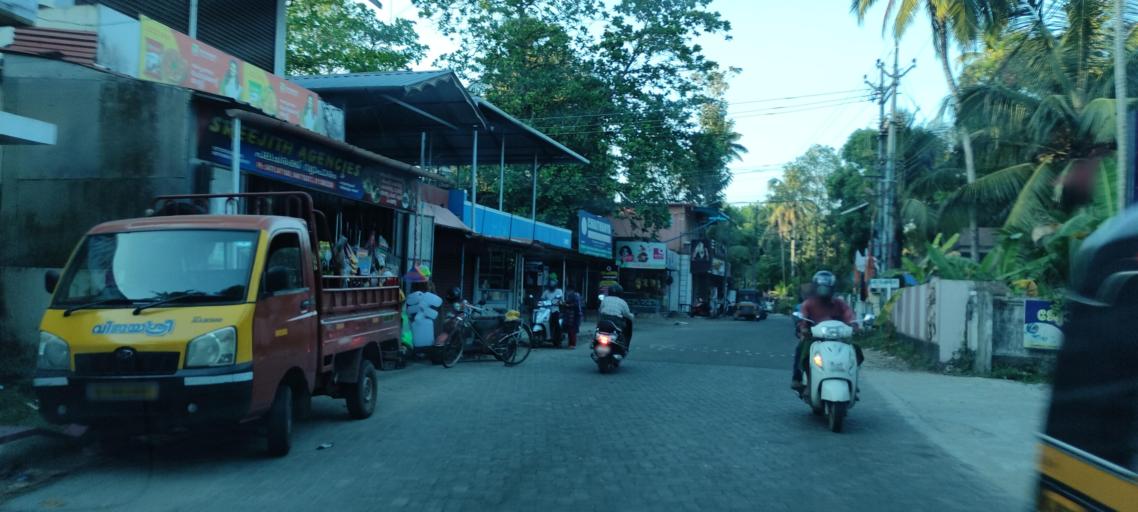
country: IN
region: Kerala
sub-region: Alappuzha
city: Kayankulam
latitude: 9.2036
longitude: 76.4631
